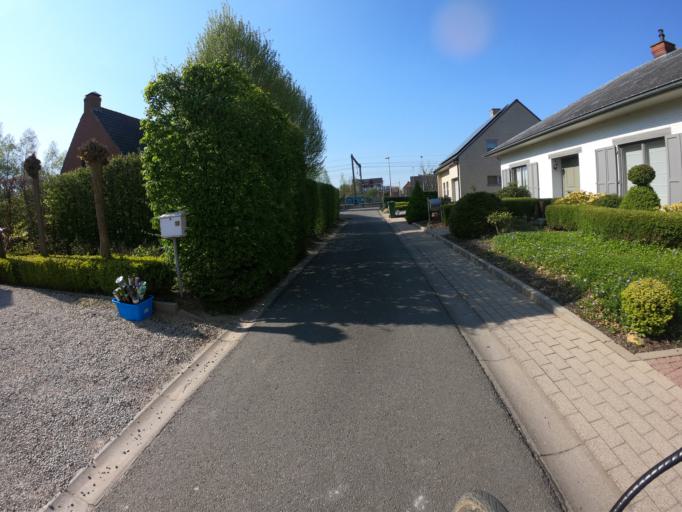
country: BE
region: Flanders
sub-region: Provincie Vlaams-Brabant
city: Galmaarden
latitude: 50.8119
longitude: 3.9707
